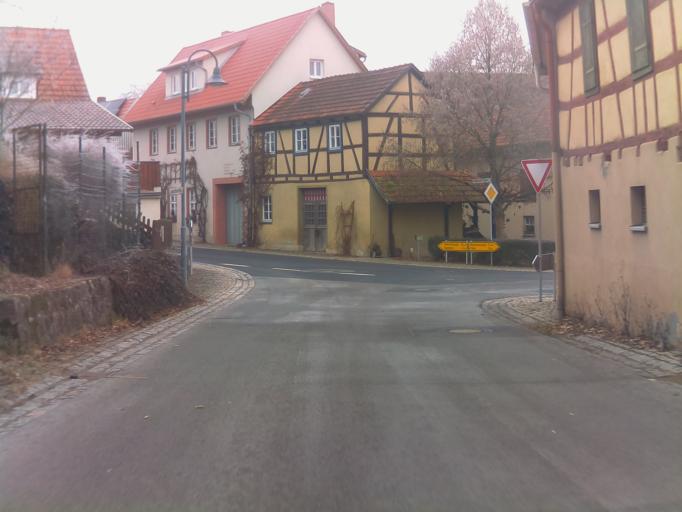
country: DE
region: Bavaria
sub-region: Regierungsbezirk Unterfranken
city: Willmars
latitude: 50.5003
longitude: 10.2433
